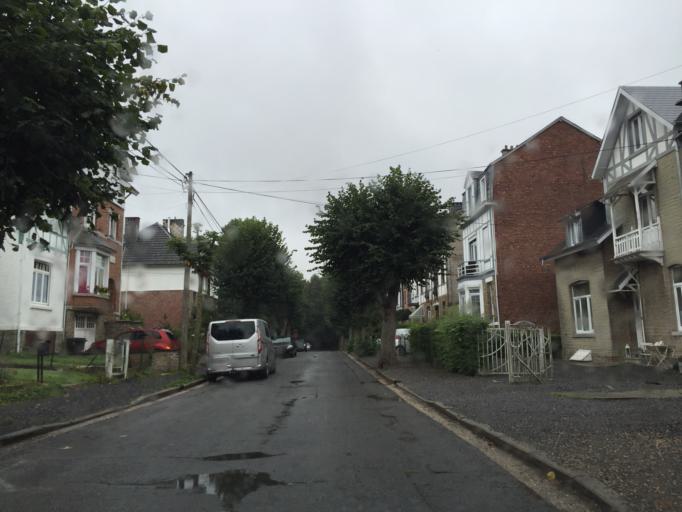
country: BE
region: Wallonia
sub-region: Province de Liege
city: Spa
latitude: 50.4870
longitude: 5.8669
